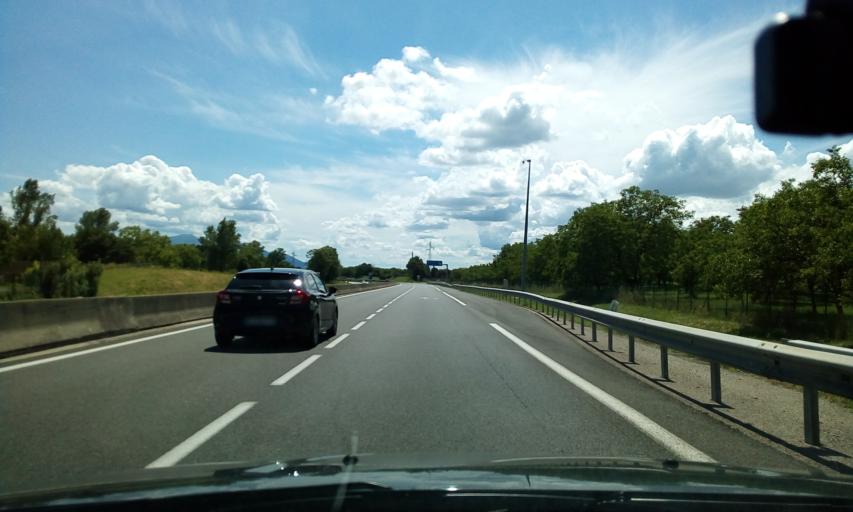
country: FR
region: Rhone-Alpes
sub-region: Departement de l'Isere
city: Saint-Sauveur
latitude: 45.1623
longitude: 5.3660
